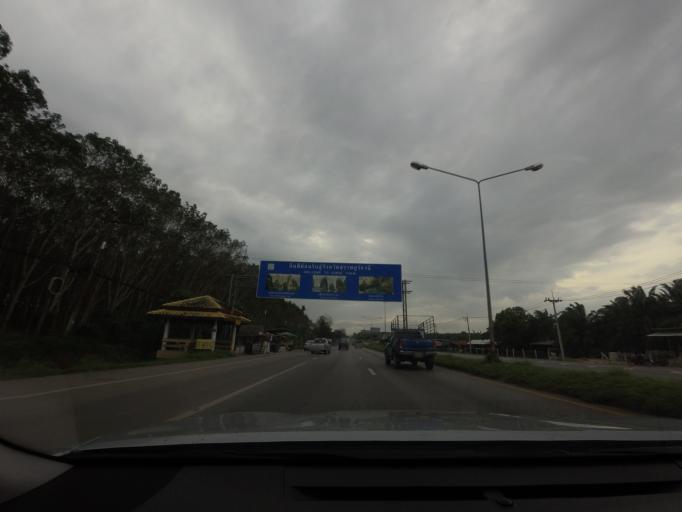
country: TH
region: Surat Thani
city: Phunphin
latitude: 9.0488
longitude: 99.1614
